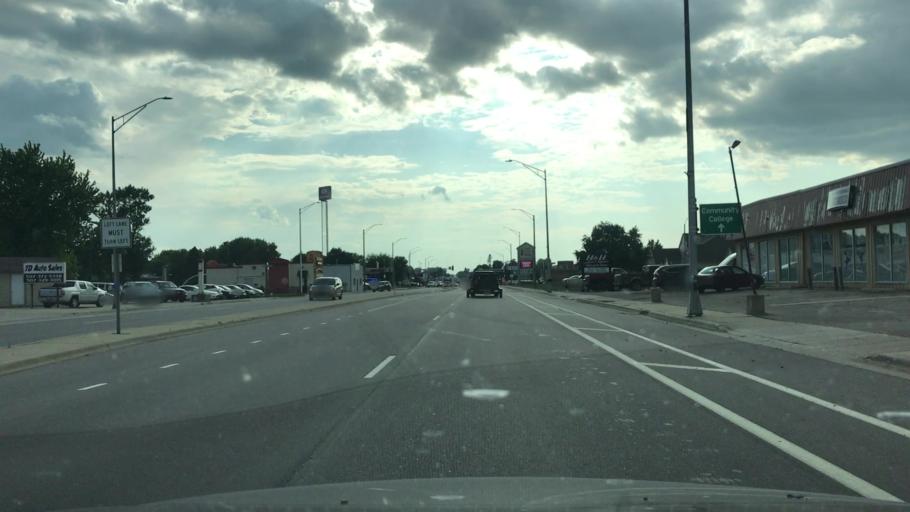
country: US
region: Minnesota
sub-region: Nobles County
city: Worthington
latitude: 43.6313
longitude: -95.5900
